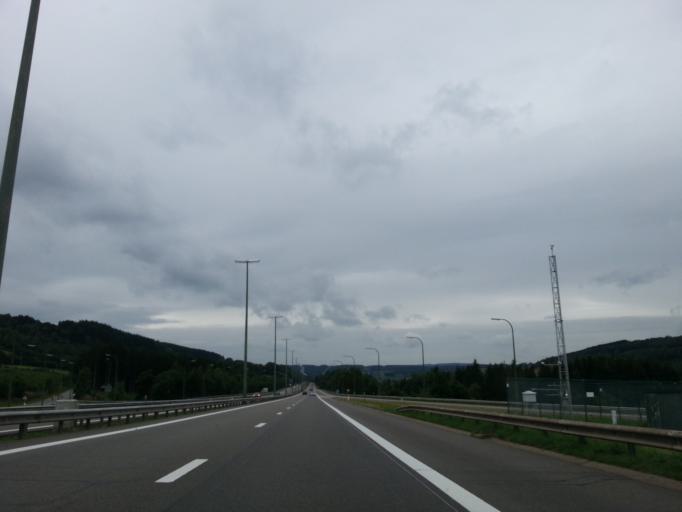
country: BE
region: Wallonia
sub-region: Province de Liege
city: Malmedy
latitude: 50.3678
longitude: 6.0253
